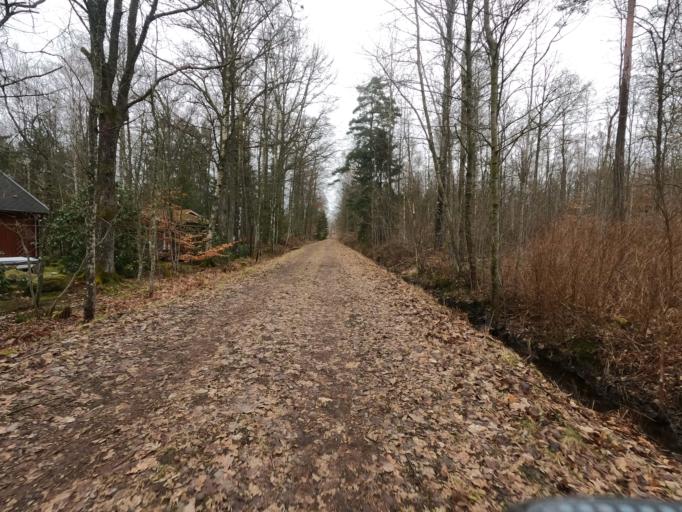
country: SE
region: Kronoberg
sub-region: Ljungby Kommun
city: Ljungby
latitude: 56.8111
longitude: 13.6896
